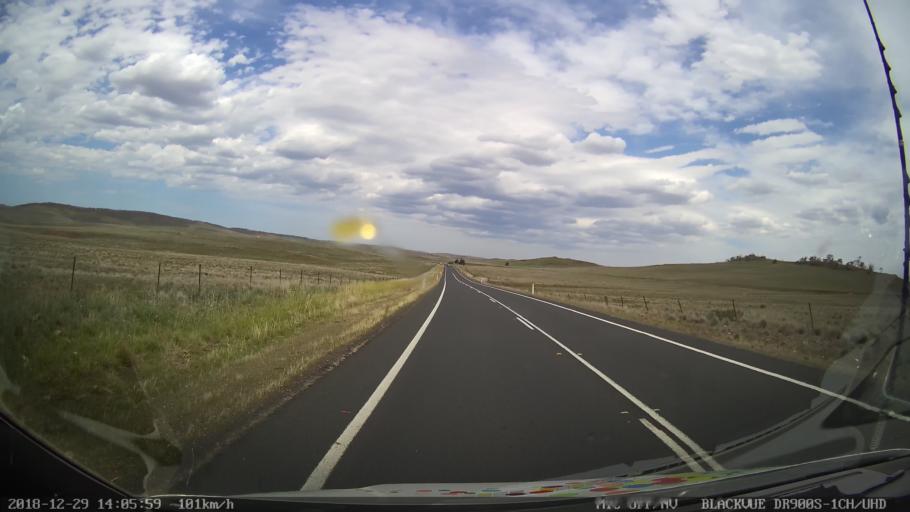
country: AU
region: New South Wales
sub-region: Cooma-Monaro
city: Cooma
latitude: -36.3382
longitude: 149.1959
